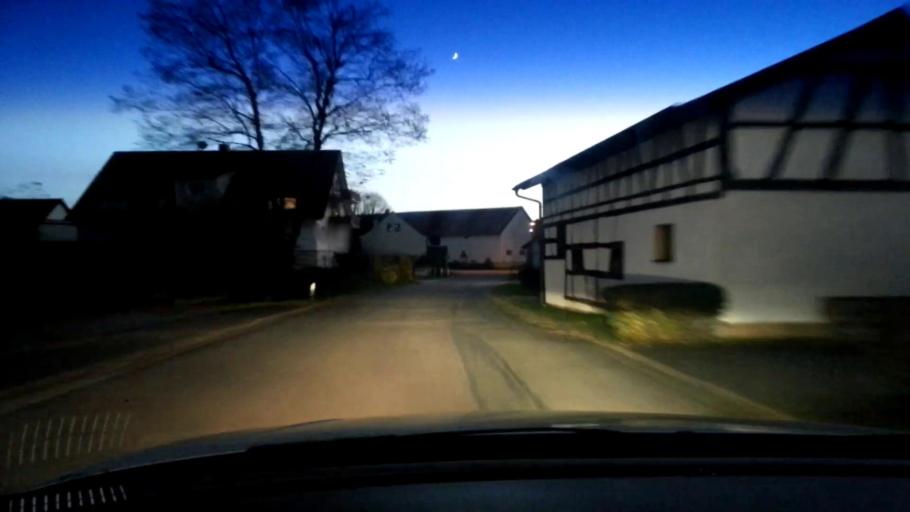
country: DE
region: Bavaria
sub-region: Upper Franconia
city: Litzendorf
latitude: 49.9416
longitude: 10.9980
